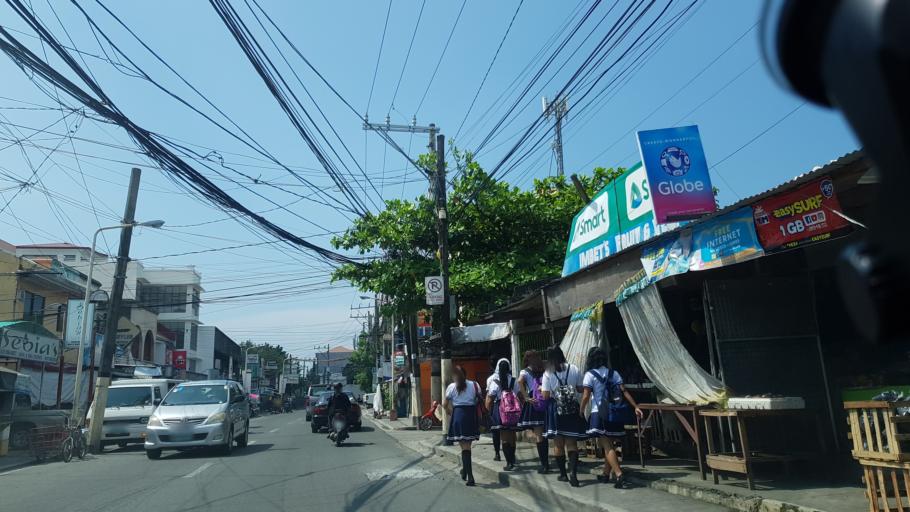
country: PH
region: Calabarzon
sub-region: Province of Rizal
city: Las Pinas
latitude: 14.4682
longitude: 120.9809
